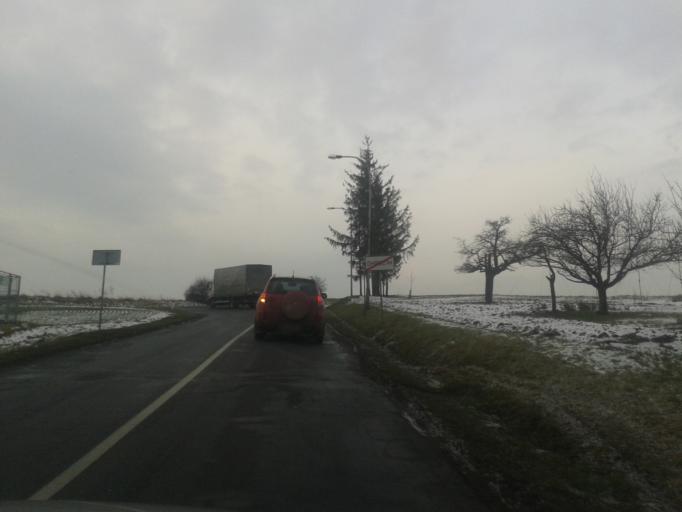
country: CZ
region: Olomoucky
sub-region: Okres Prostejov
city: Plumlov
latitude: 49.4839
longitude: 17.0165
